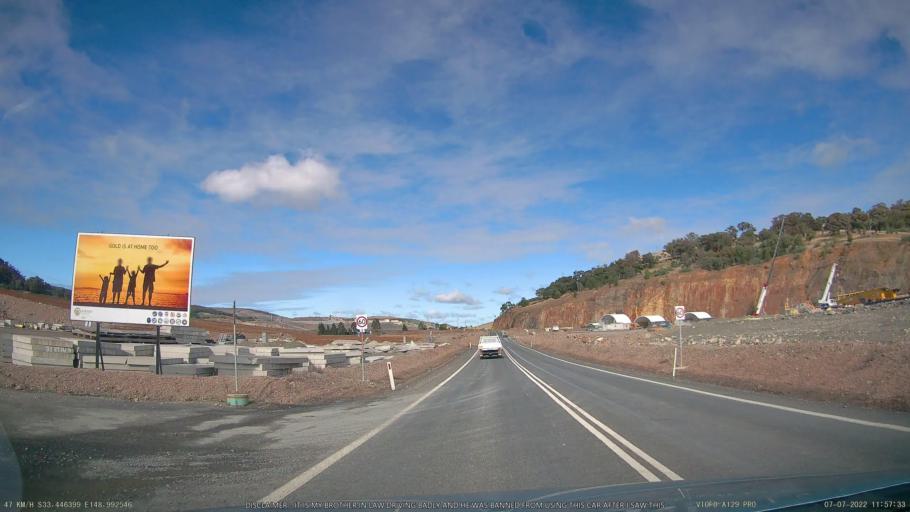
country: AU
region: New South Wales
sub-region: Blayney
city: Millthorpe
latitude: -33.4466
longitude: 148.9921
